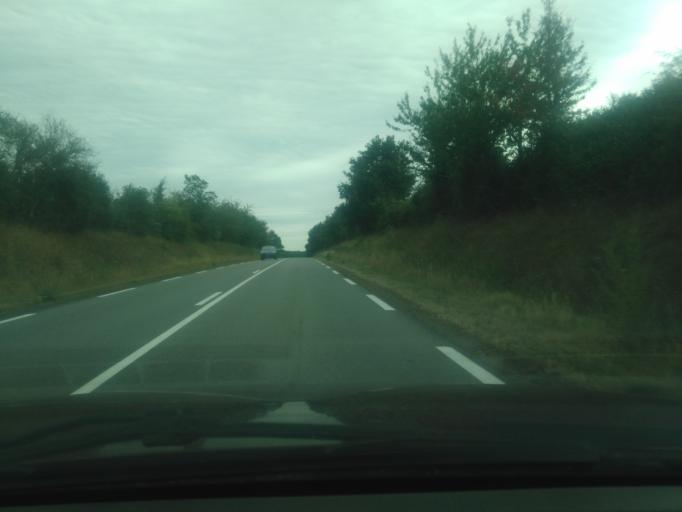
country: FR
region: Centre
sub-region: Departement de l'Indre
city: Neuvy-Saint-Sepulchre
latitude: 46.5805
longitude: 1.8388
